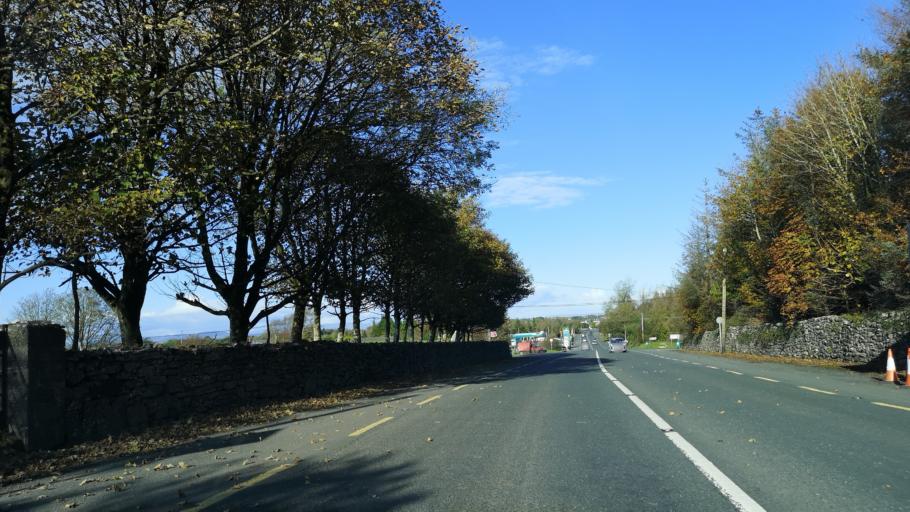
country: IE
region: Connaught
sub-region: County Galway
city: Moycullen
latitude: 53.4483
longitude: -9.0895
